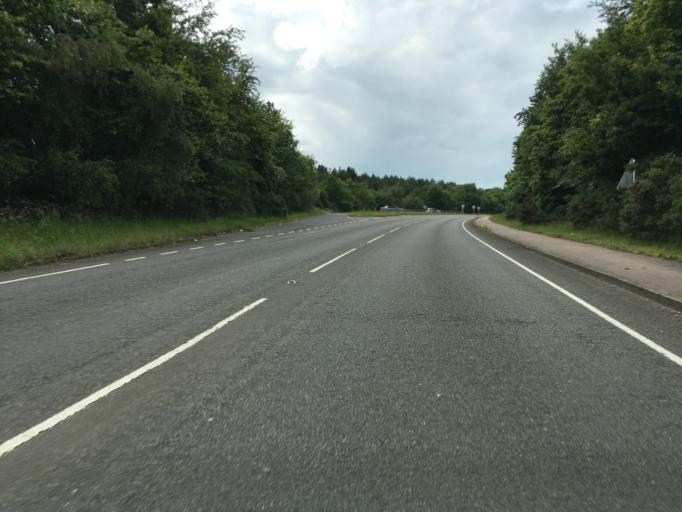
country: GB
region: England
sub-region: Central Bedfordshire
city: Aspley Guise
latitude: 51.9996
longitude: -0.6395
